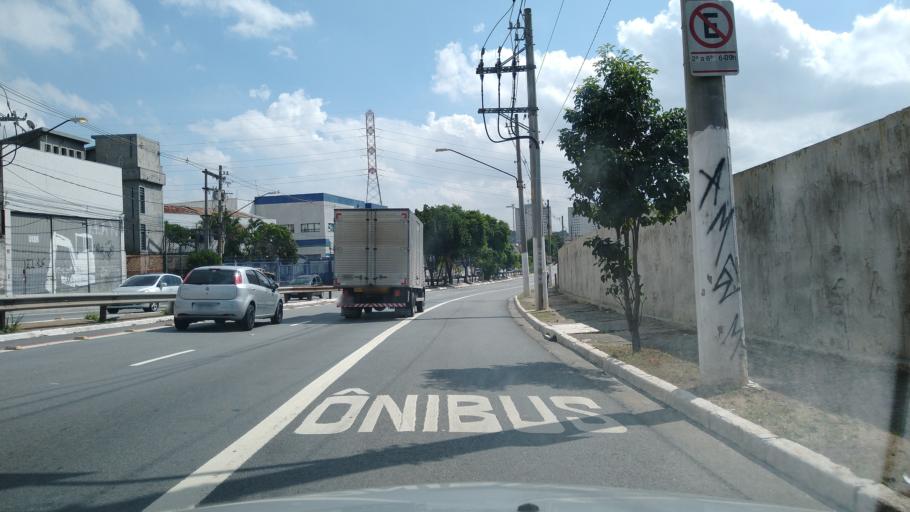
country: BR
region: Sao Paulo
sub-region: Guarulhos
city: Guarulhos
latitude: -23.4858
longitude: -46.4840
